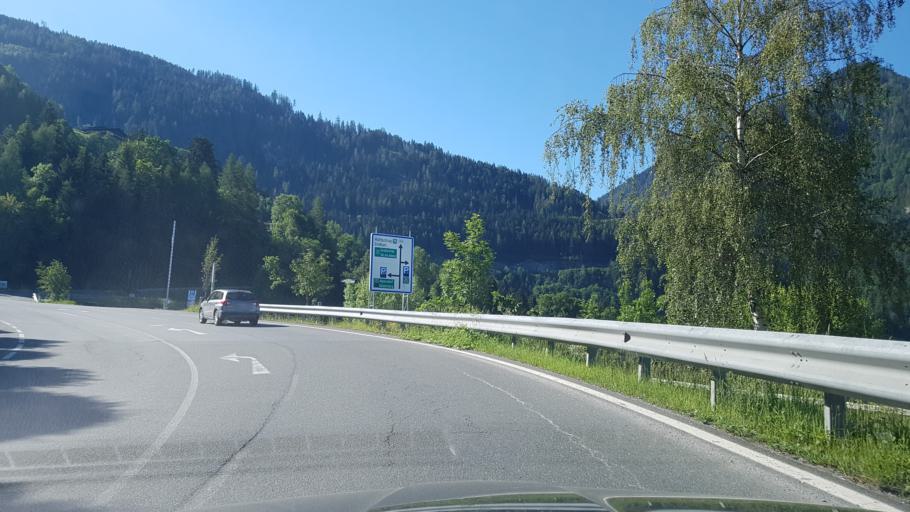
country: AT
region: Salzburg
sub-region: Politischer Bezirk Sankt Johann im Pongau
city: Sankt Johann im Pongau
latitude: 47.3220
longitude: 13.1936
